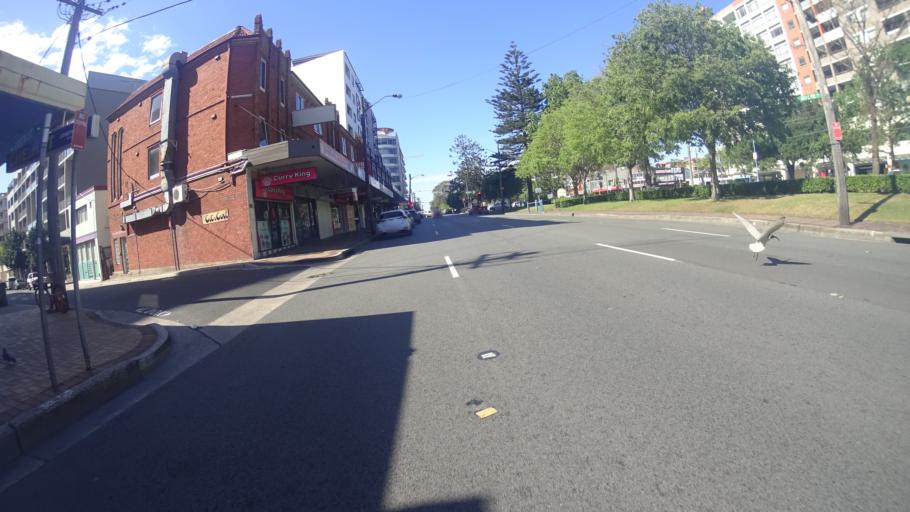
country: AU
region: New South Wales
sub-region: Randwick
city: Daceyville
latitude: -33.9408
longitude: 151.2393
